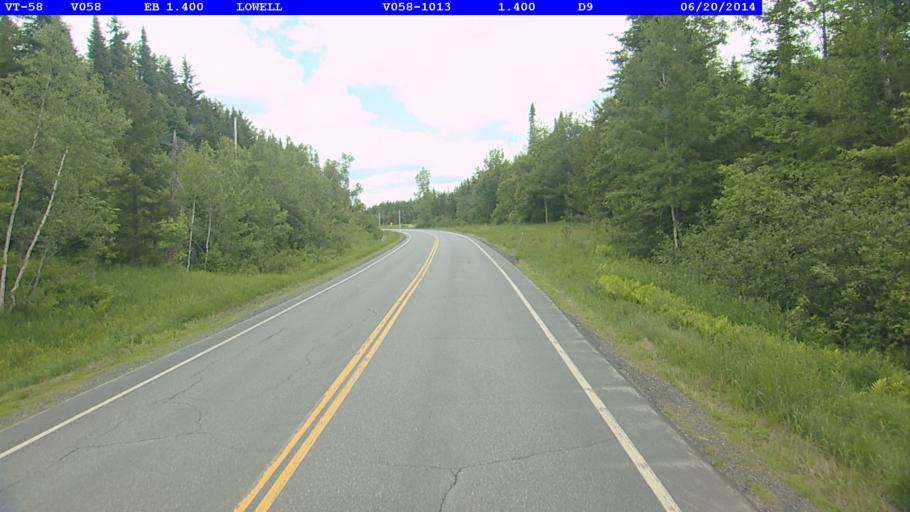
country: US
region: Vermont
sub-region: Orleans County
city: Newport
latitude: 44.7993
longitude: -72.4217
